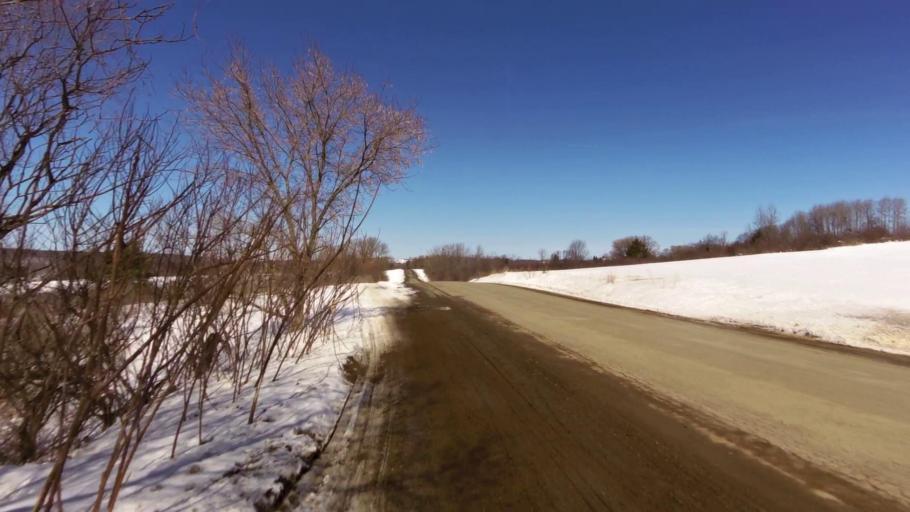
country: US
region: New York
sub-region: Allegany County
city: Houghton
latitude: 42.4304
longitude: -78.3086
